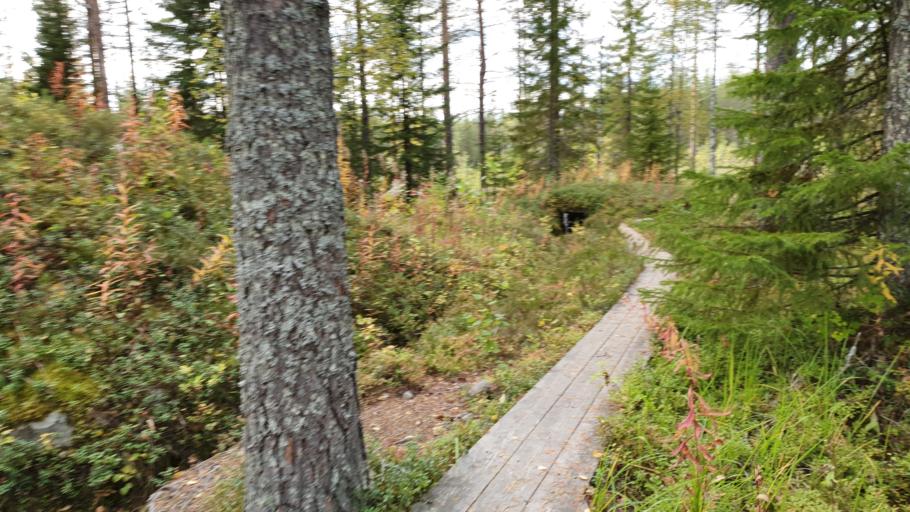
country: FI
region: North Karelia
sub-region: Pielisen Karjala
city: Lieksa
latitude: 63.9213
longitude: 30.1406
